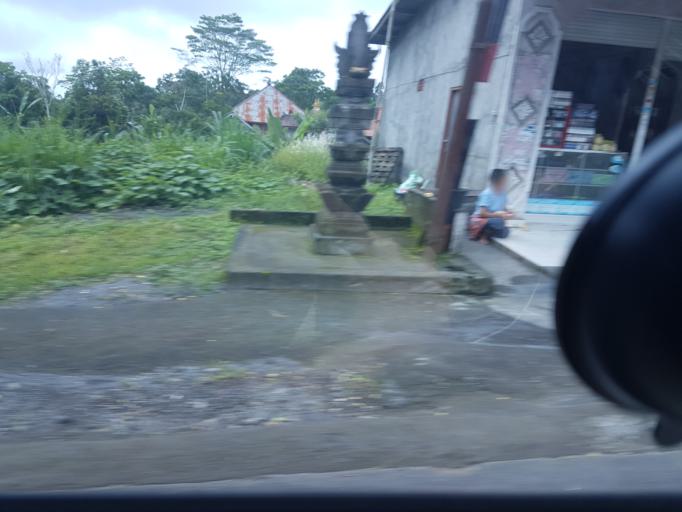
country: ID
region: Bali
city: Banjar Kedisan
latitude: -8.3027
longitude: 115.3541
